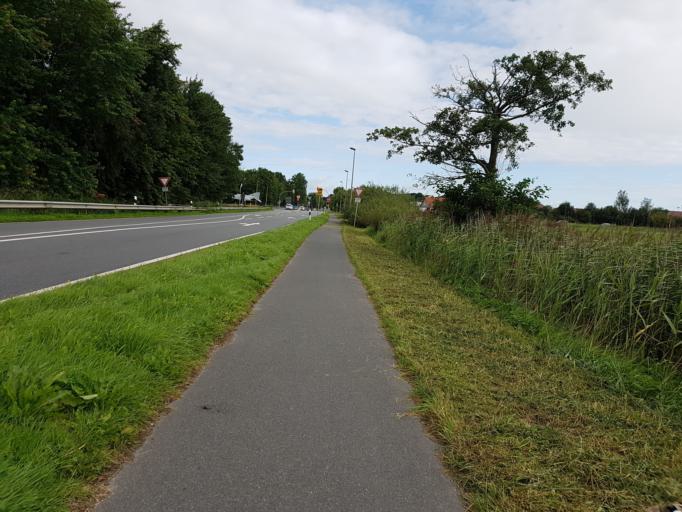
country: DE
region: Lower Saxony
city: Wittmund
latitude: 53.5664
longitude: 7.7838
